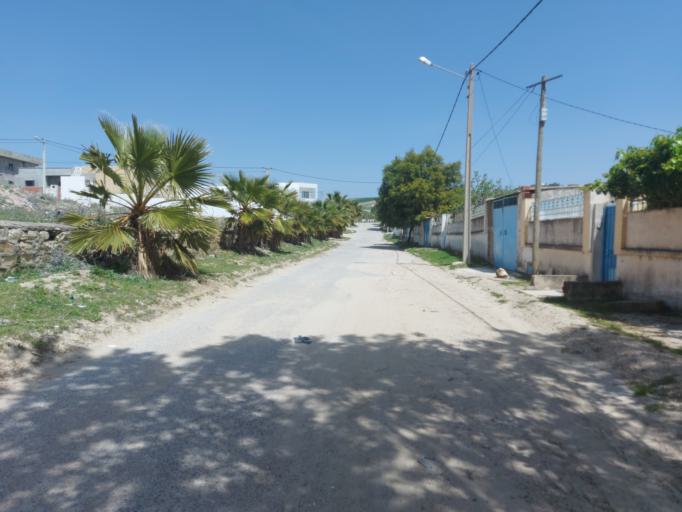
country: TN
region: Kef
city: El Kef
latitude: 36.1824
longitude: 8.7289
